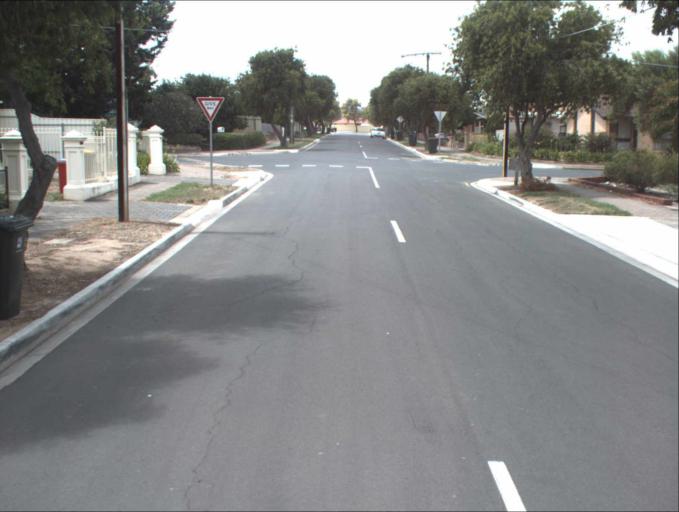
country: AU
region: South Australia
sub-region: Port Adelaide Enfield
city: Gilles Plains
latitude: -34.8567
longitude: 138.6637
